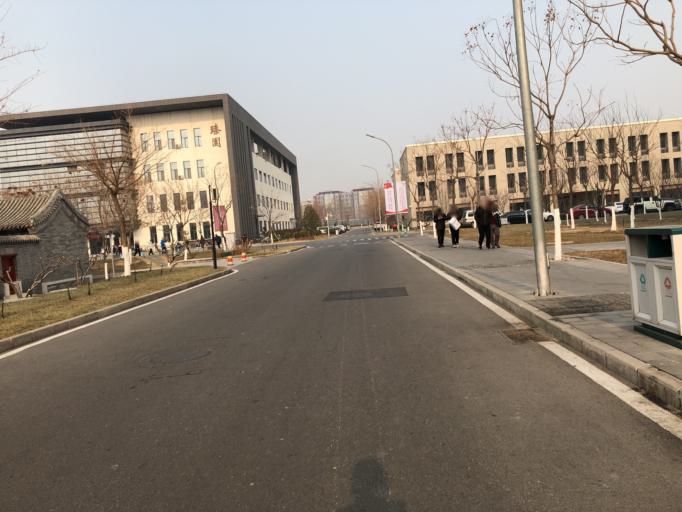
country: CN
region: Beijing
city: Daxing
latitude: 39.7464
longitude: 116.2825
